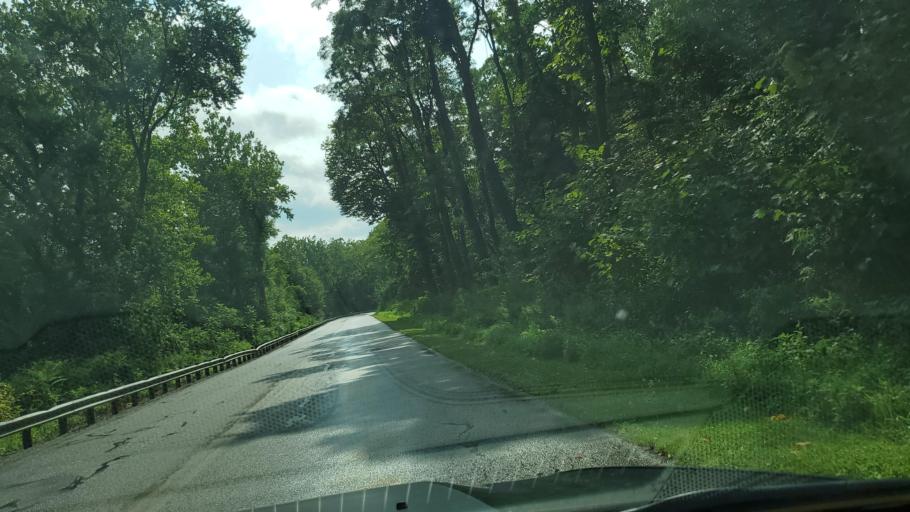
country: US
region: Ohio
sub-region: Mahoning County
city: Lowellville
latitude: 41.0411
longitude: -80.5495
